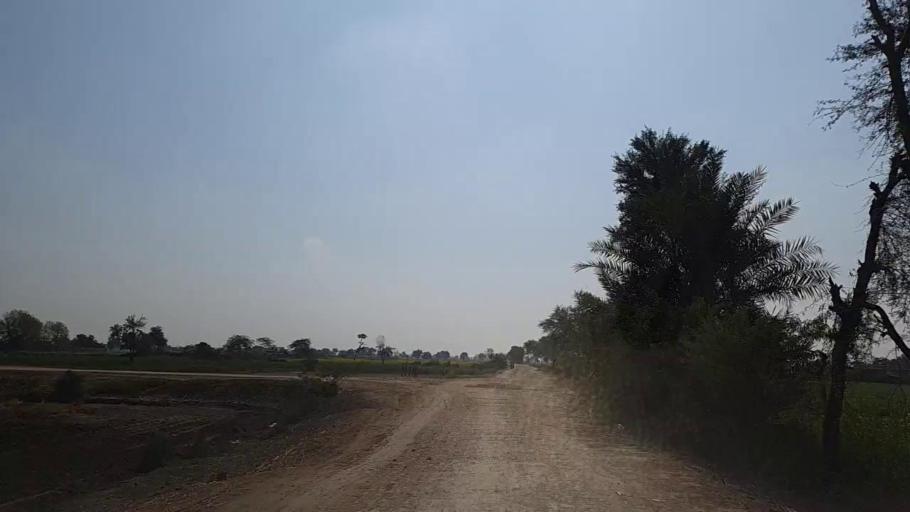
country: PK
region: Sindh
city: Daur
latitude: 26.4556
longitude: 68.2631
